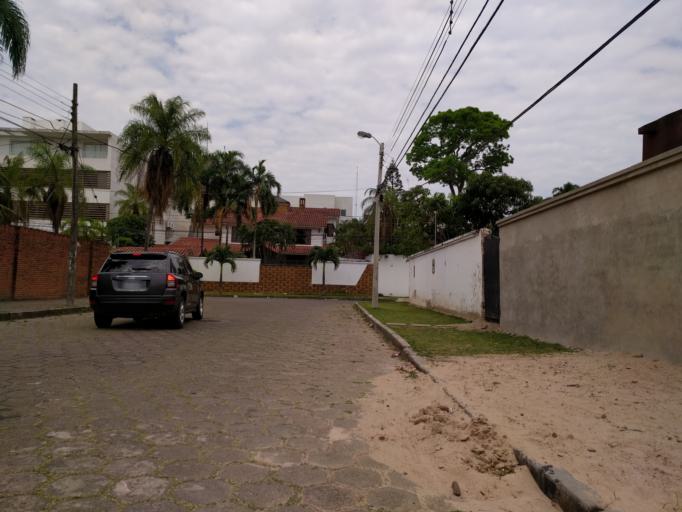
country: BO
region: Santa Cruz
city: Santa Cruz de la Sierra
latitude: -17.7996
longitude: -63.2145
